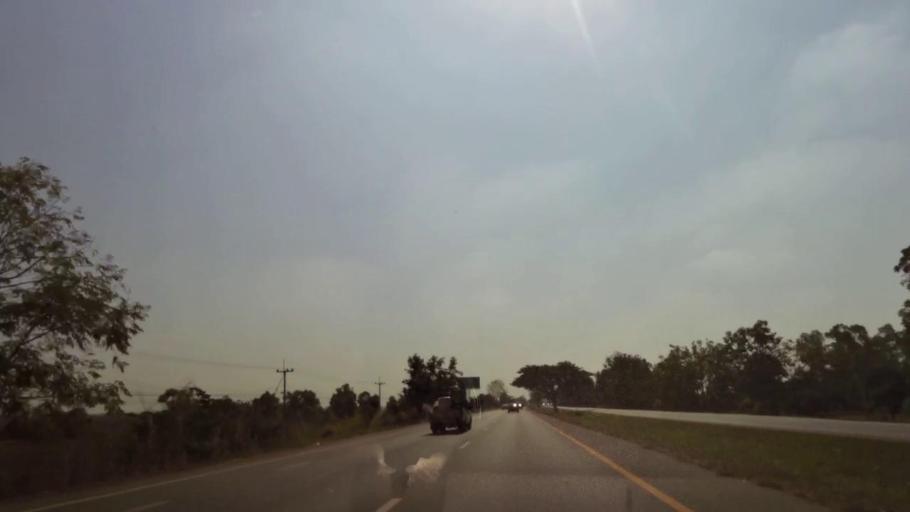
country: TH
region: Phichit
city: Wachira Barami
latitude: 16.4689
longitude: 100.1474
